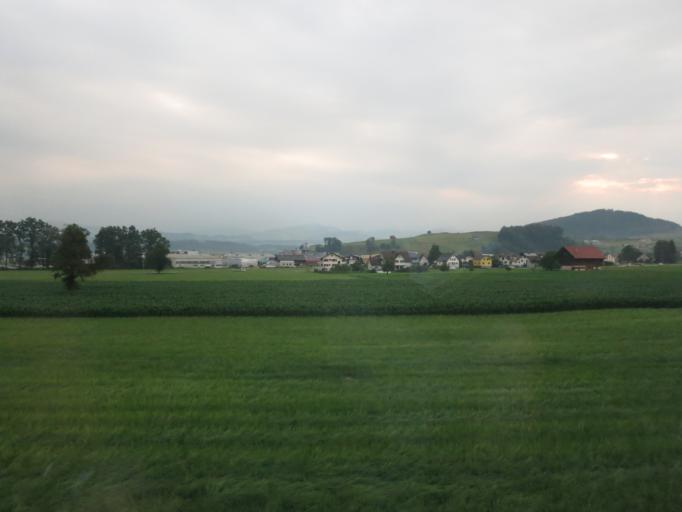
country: CH
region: Schwyz
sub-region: Bezirk March
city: Lachen
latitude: 47.1901
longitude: 8.8775
